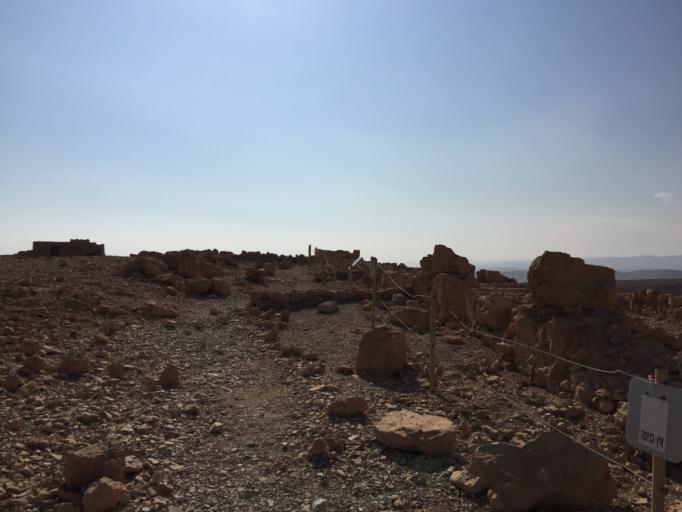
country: IL
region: Southern District
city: `En Boqeq
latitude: 31.3136
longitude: 35.3526
